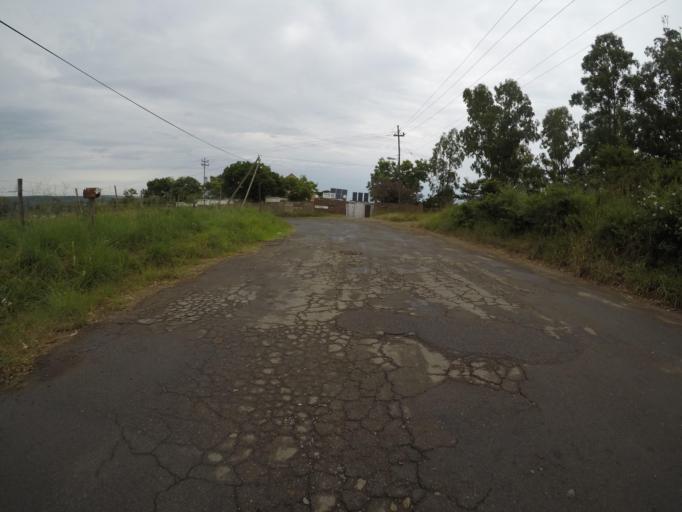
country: ZA
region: Eastern Cape
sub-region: Buffalo City Metropolitan Municipality
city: East London
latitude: -32.9611
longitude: 27.8407
